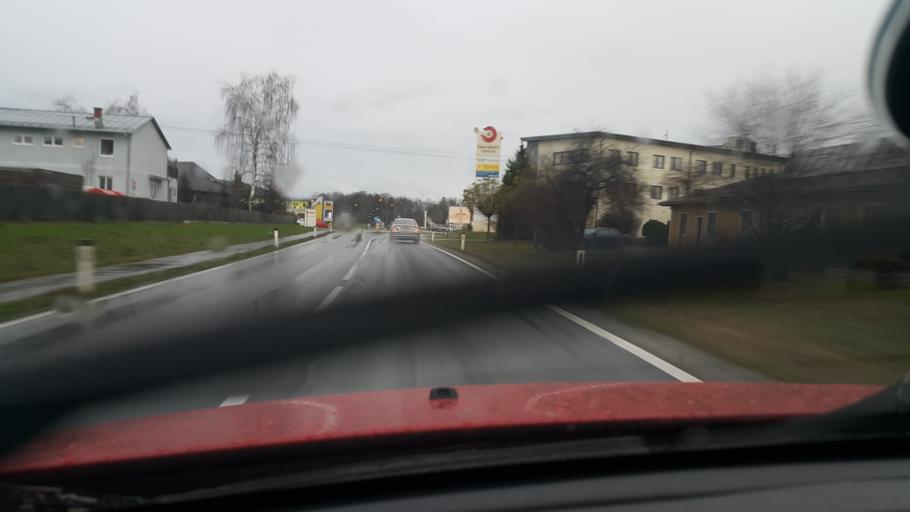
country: AT
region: Styria
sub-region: Politischer Bezirk Deutschlandsberg
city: Preding
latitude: 46.8536
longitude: 15.4129
